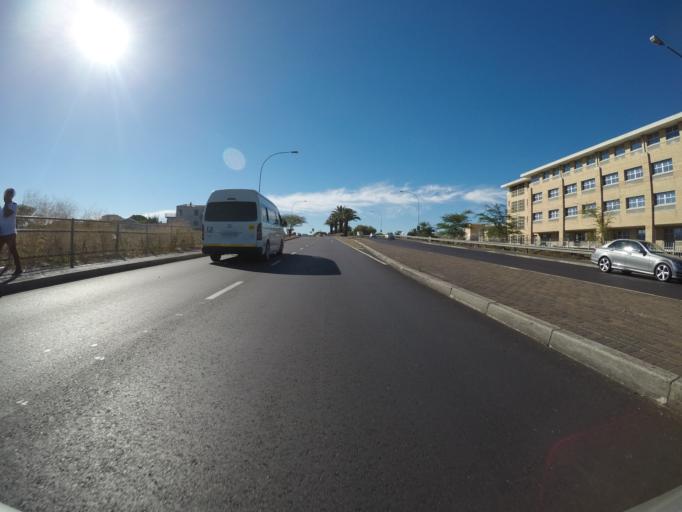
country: ZA
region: Western Cape
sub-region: City of Cape Town
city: Kraaifontein
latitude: -33.9194
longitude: 18.6747
